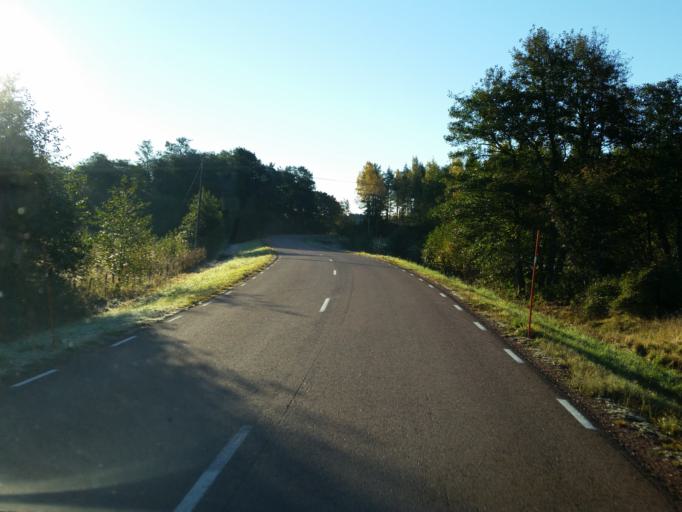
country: AX
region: Alands skaergard
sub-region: Vardoe
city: Vardoe
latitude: 60.2364
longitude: 20.3743
